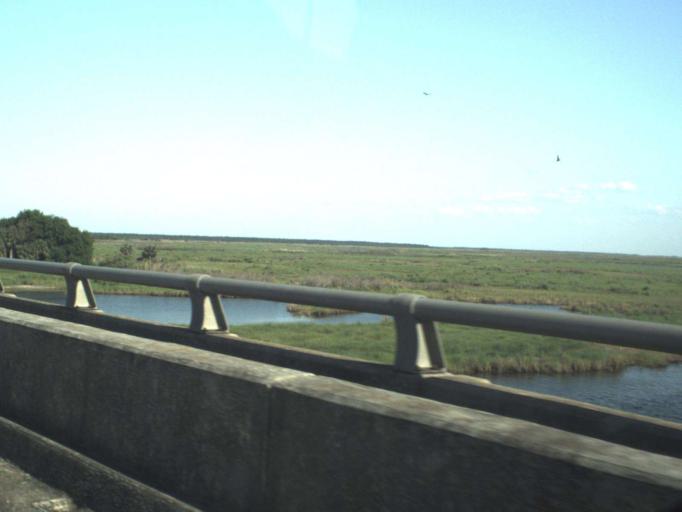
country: US
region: Florida
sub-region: Seminole County
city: Geneva
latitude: 28.7141
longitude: -81.0343
